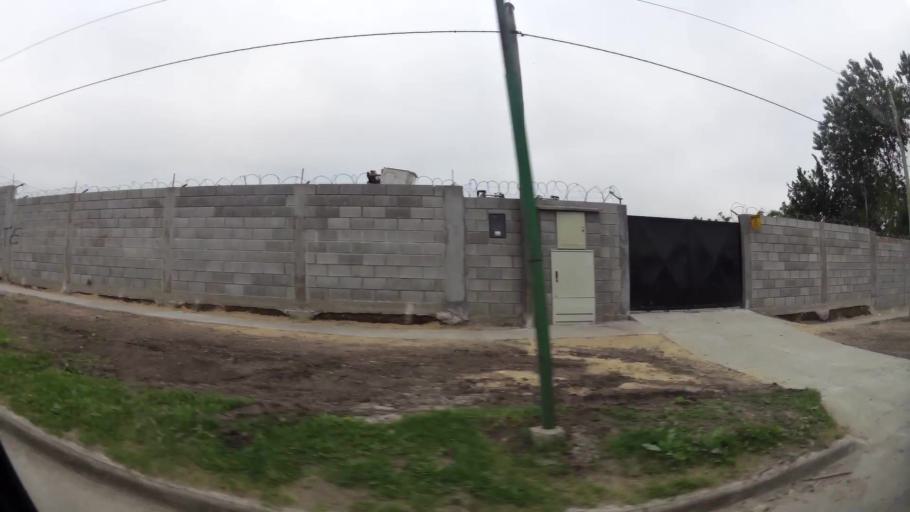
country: AR
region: Buenos Aires
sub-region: Partido de La Plata
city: La Plata
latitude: -34.9383
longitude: -58.0015
